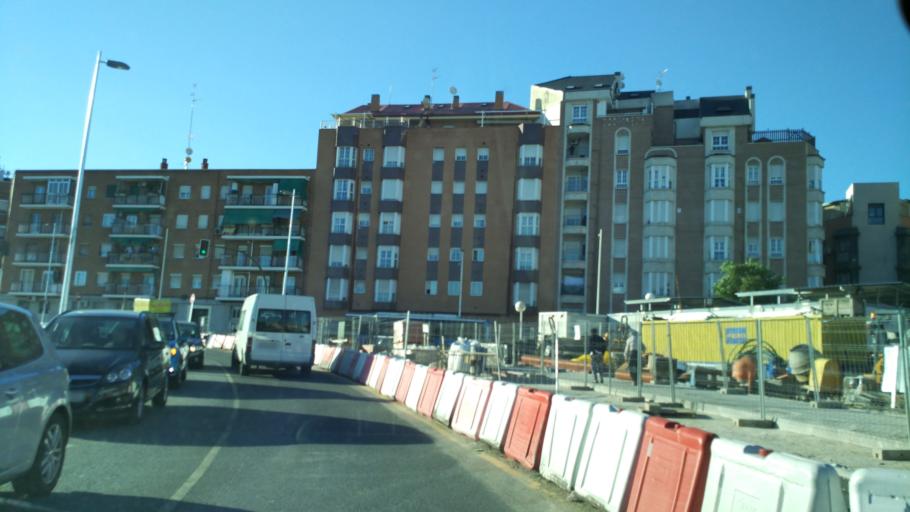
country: ES
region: Madrid
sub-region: Provincia de Madrid
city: Tetuan de las Victorias
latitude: 40.4645
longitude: -3.7063
